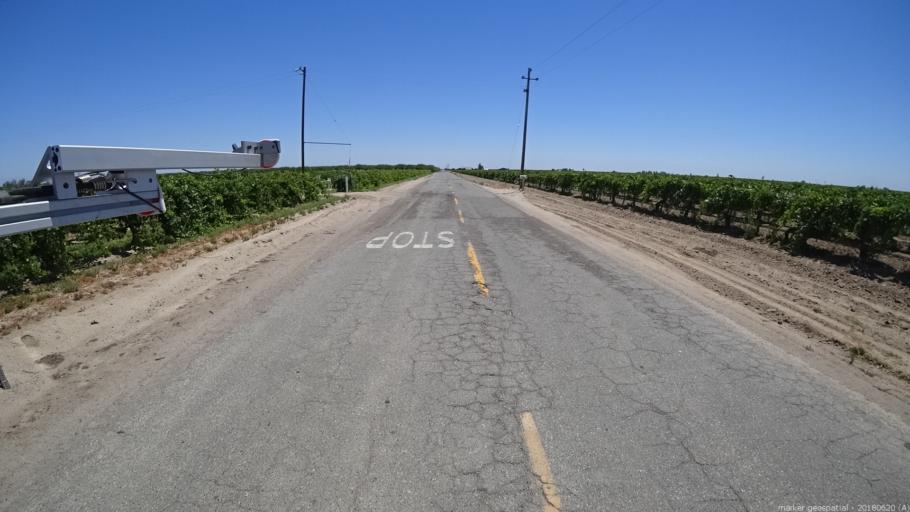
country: US
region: California
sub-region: Madera County
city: Parkwood
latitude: 36.8803
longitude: -120.0355
